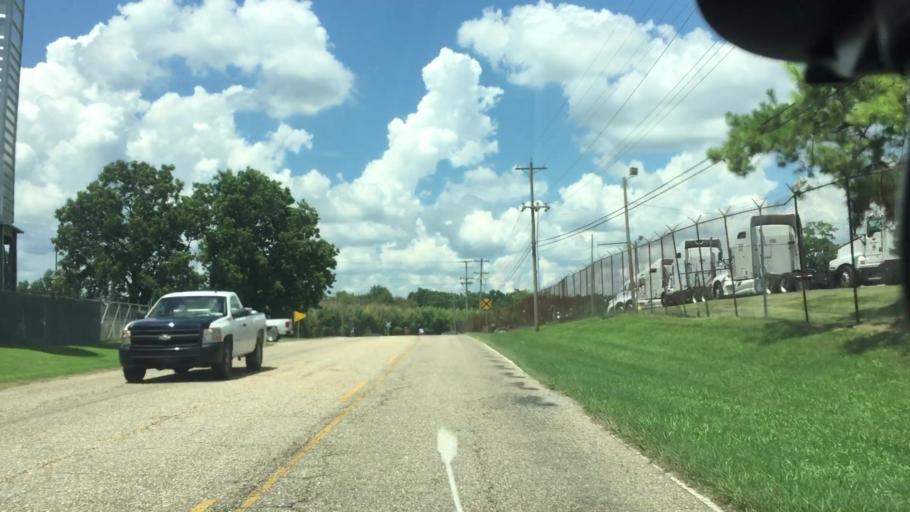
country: US
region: Alabama
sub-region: Pike County
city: Troy
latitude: 31.7842
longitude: -85.9807
